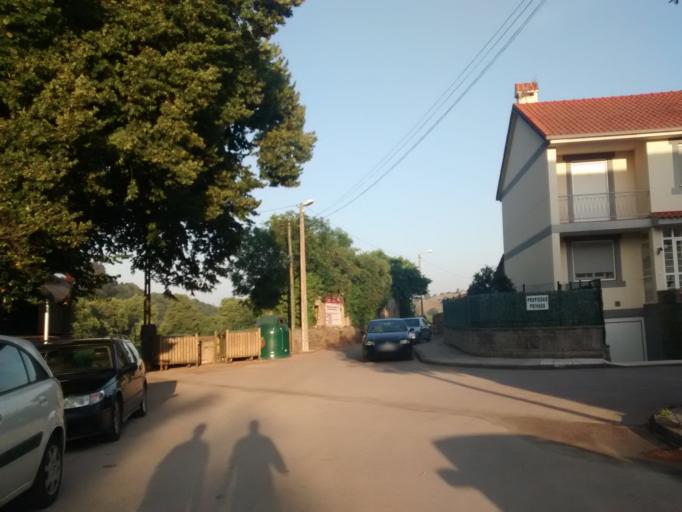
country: ES
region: Cantabria
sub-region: Provincia de Cantabria
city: Entrambasaguas
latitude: 43.3795
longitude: -3.7208
